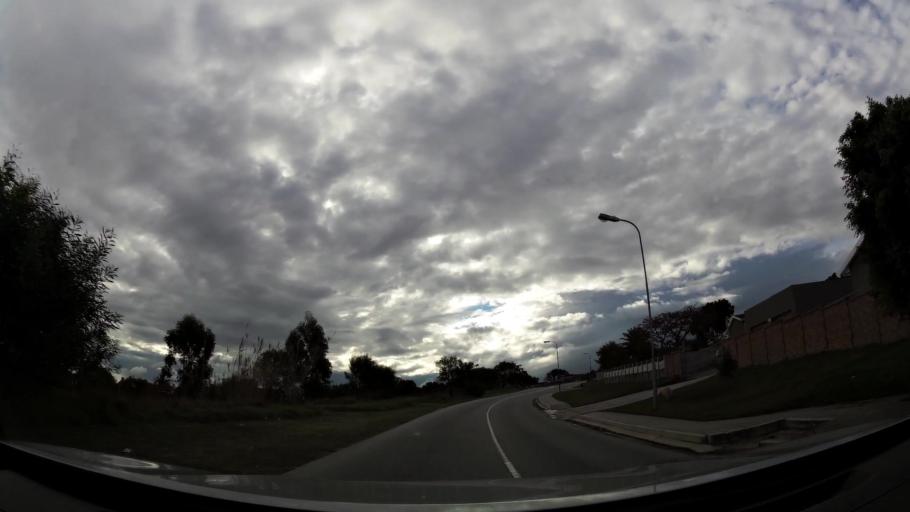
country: ZA
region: Eastern Cape
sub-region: Nelson Mandela Bay Metropolitan Municipality
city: Port Elizabeth
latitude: -33.9517
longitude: 25.5054
